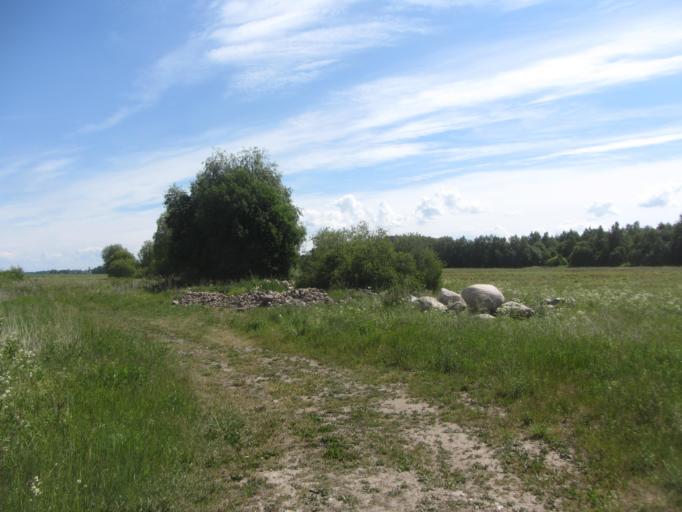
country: LT
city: Obeliai
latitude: 56.1140
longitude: 25.0801
